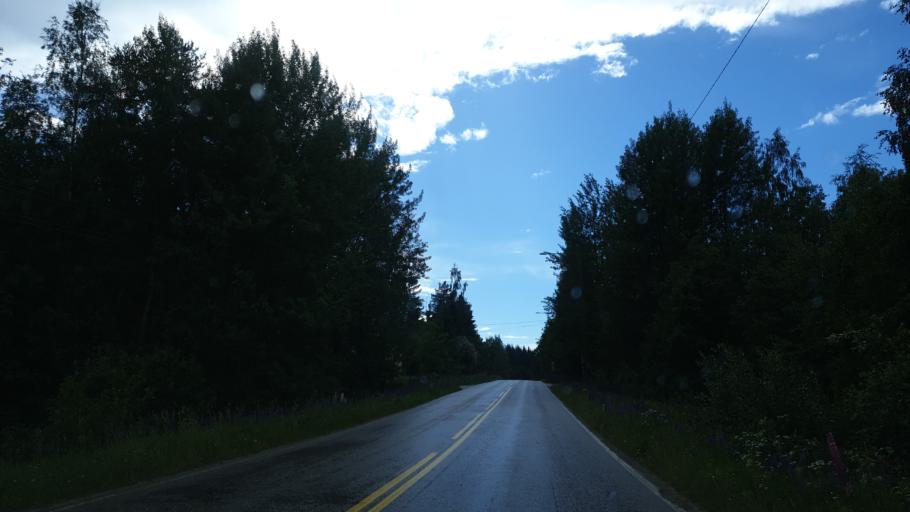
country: FI
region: Northern Savo
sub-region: Kuopio
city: Kuopio
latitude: 62.9085
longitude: 27.8593
